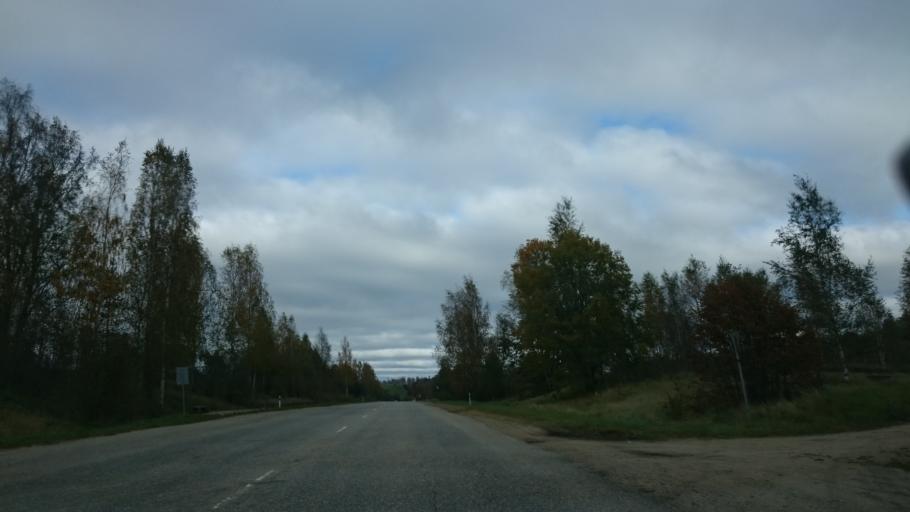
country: LV
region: Amatas Novads
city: Drabesi
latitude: 57.2538
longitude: 25.2631
